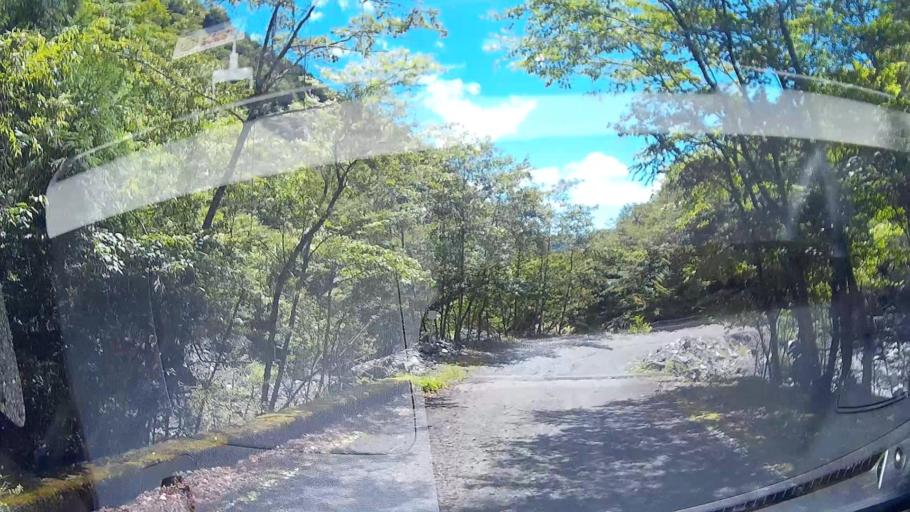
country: JP
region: Shizuoka
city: Fujinomiya
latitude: 35.2997
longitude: 138.3141
